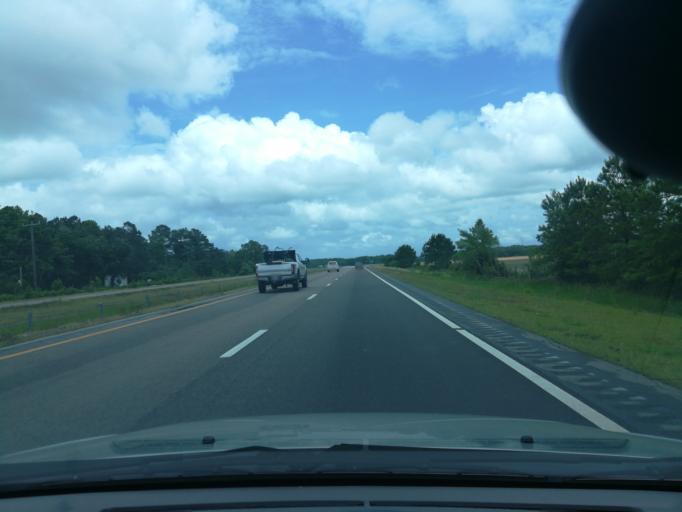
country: US
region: North Carolina
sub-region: Tyrrell County
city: Columbia
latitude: 35.8957
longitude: -76.3446
